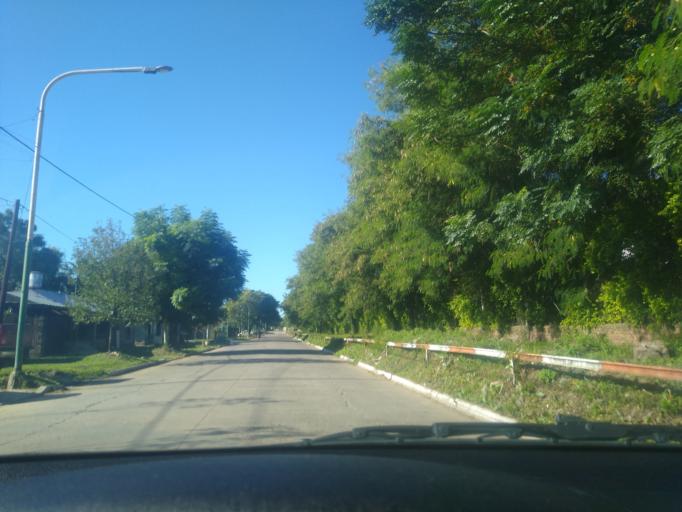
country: AR
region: Chaco
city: Puerto Vilelas
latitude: -27.5113
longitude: -58.9393
